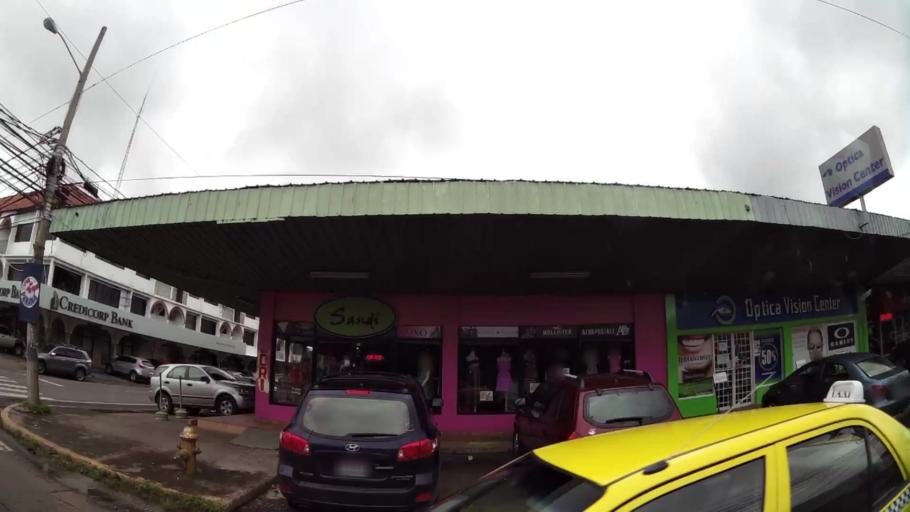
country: PA
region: Chiriqui
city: David
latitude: 8.4314
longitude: -82.4272
